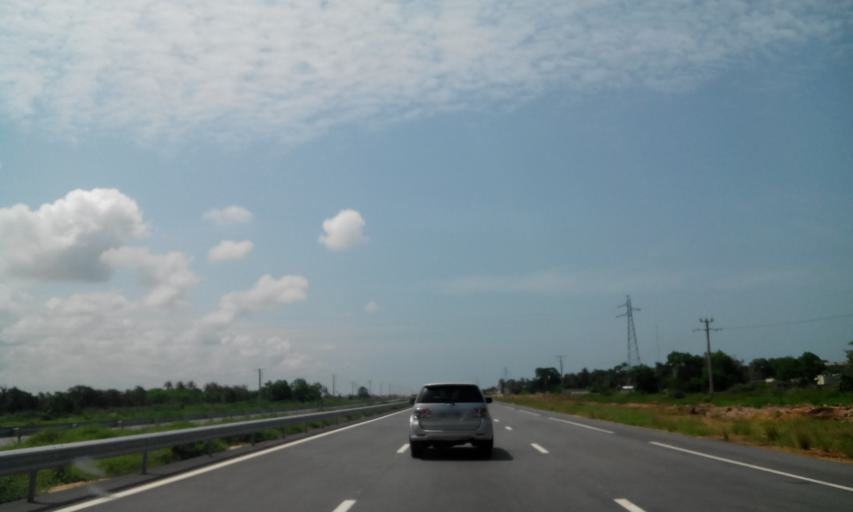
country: CI
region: Sud-Comoe
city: Grand-Bassam
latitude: 5.2330
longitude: -3.7638
